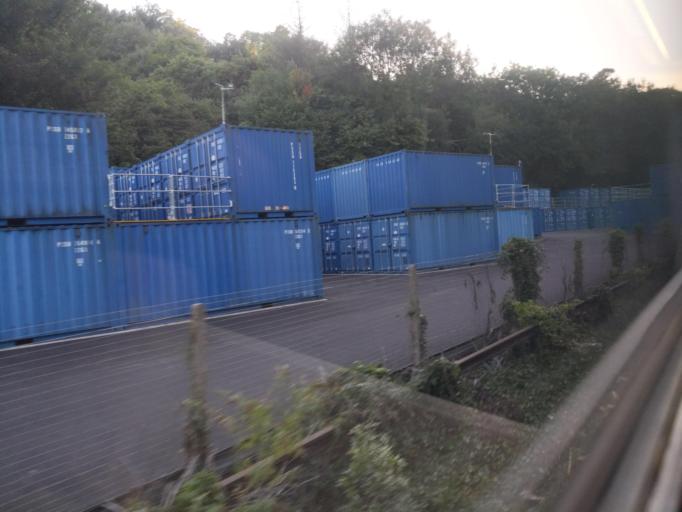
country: GB
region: England
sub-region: Borough of Torbay
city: Torquay
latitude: 50.4737
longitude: -3.5475
